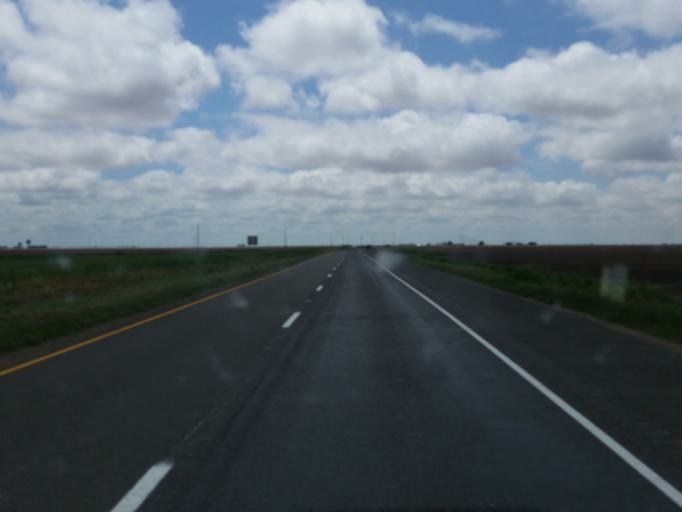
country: US
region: Texas
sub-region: Lubbock County
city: Slaton
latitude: 33.4143
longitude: -101.6338
